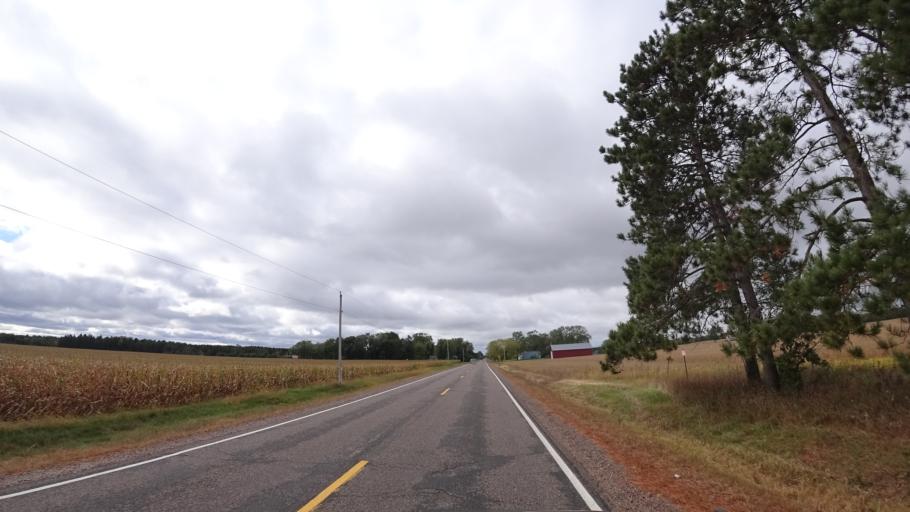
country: US
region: Wisconsin
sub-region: Chippewa County
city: Lake Wissota
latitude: 44.9806
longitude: -91.2828
